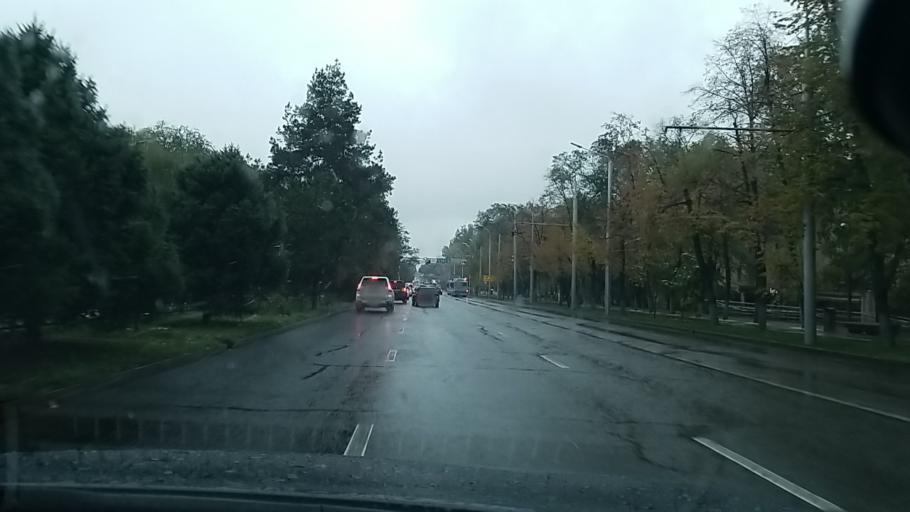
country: KZ
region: Almaty Qalasy
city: Almaty
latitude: 43.2417
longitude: 76.9367
